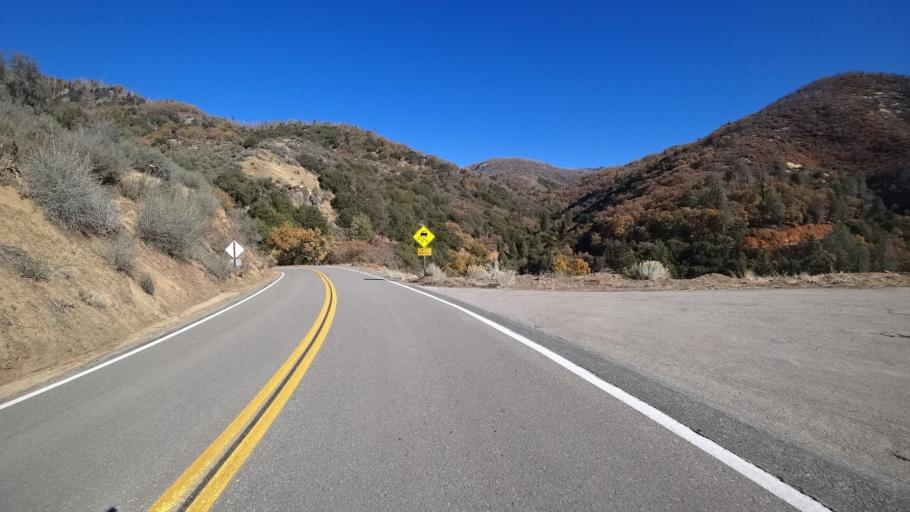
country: US
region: California
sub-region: Kern County
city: Alta Sierra
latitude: 35.7471
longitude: -118.5859
